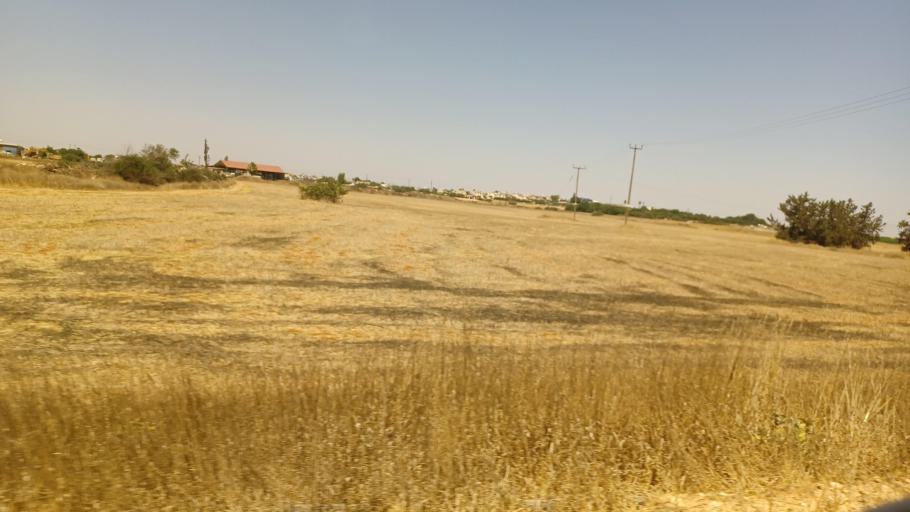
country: CY
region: Ammochostos
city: Frenaros
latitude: 35.0736
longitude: 33.8948
